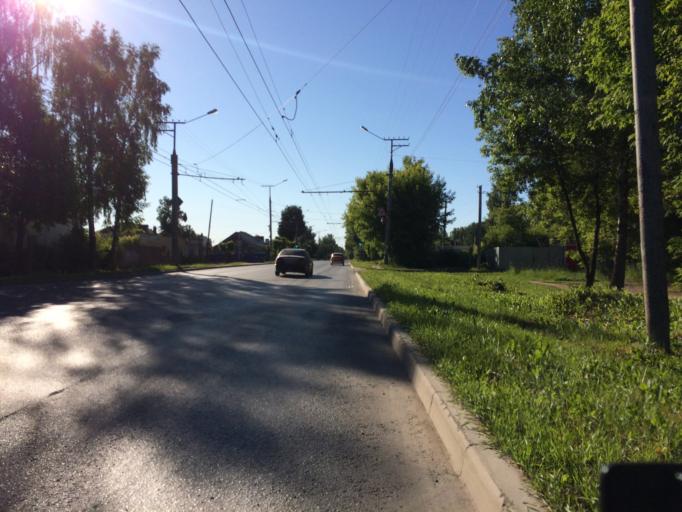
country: RU
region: Mariy-El
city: Yoshkar-Ola
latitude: 56.6524
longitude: 47.8832
